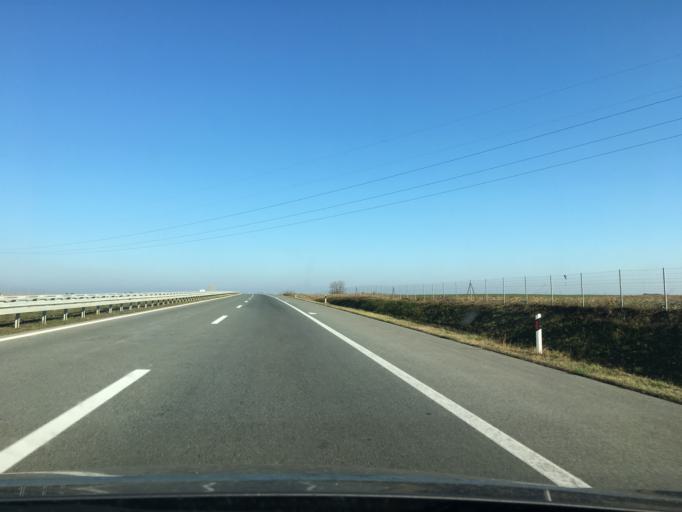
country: RS
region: Autonomna Pokrajina Vojvodina
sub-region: Severnobacki Okrug
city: Mali Igos
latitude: 45.6538
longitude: 19.7227
